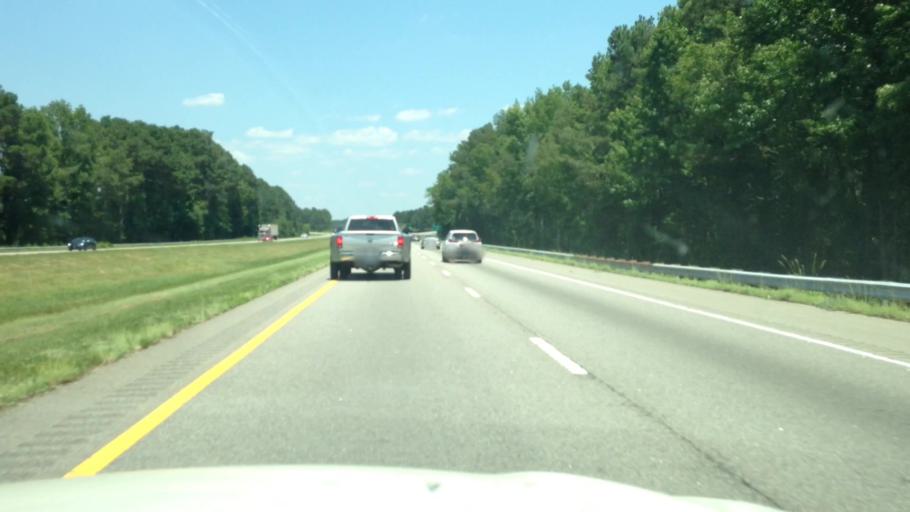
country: US
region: North Carolina
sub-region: Robeson County
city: Rowland
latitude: 34.5483
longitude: -79.2086
